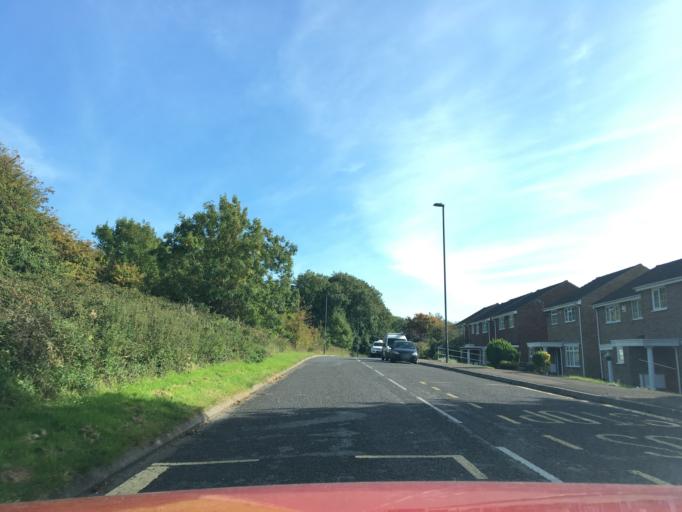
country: GB
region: England
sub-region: South Gloucestershire
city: Chipping Sodbury
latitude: 51.5504
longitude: -2.4038
